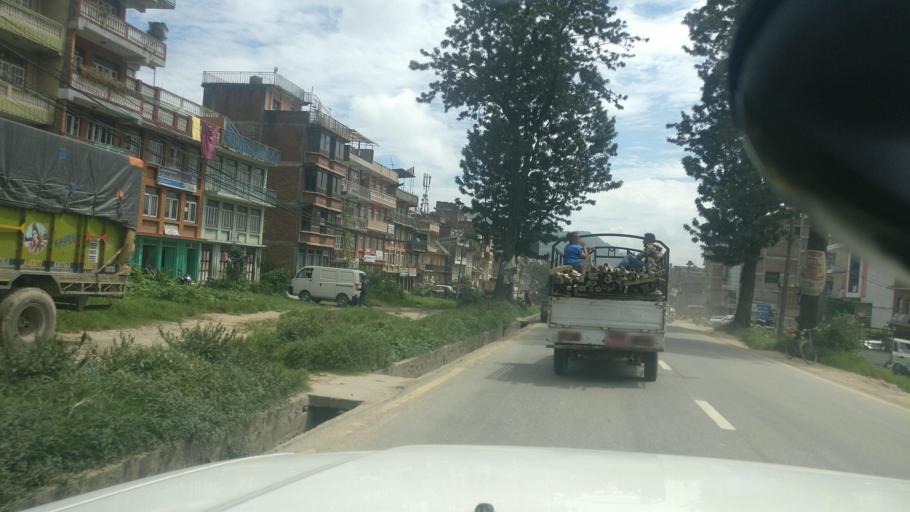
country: NP
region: Central Region
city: Banepa
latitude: 27.6323
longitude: 85.5117
